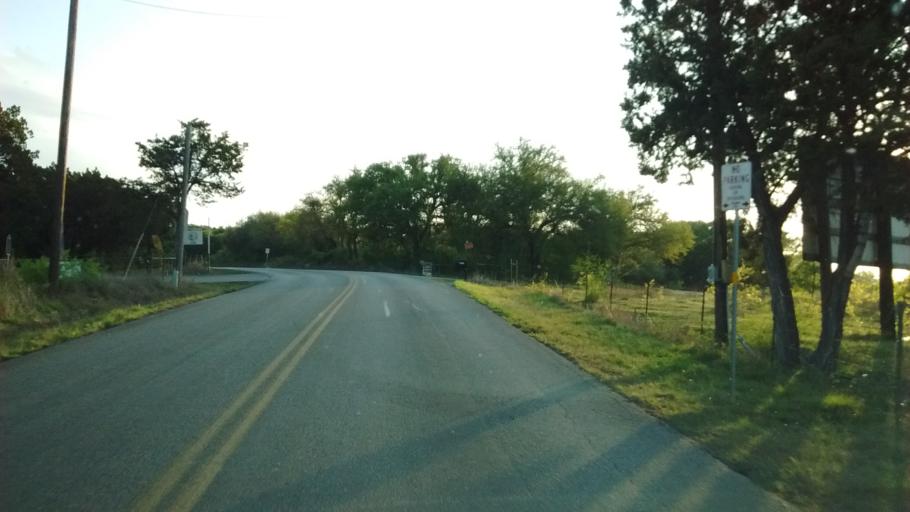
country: US
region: Texas
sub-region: Comal County
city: New Braunfels
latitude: 29.7537
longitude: -98.1432
